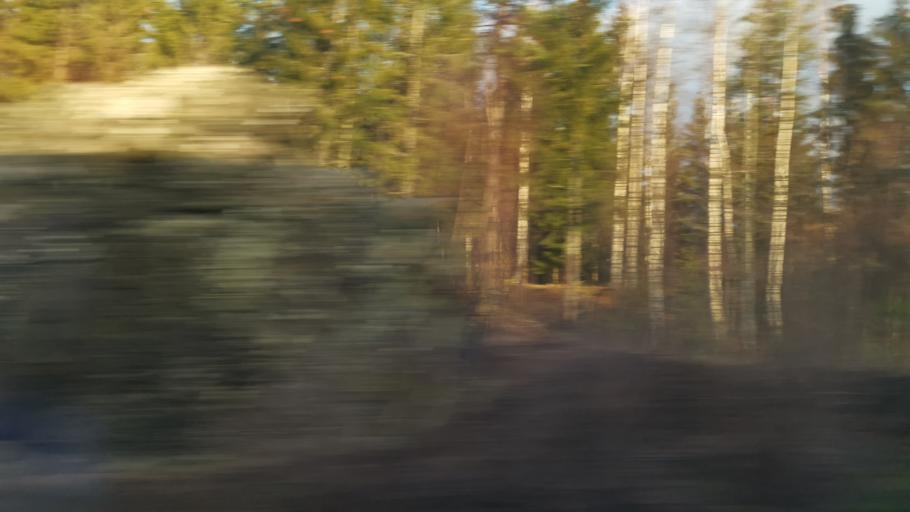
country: SE
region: Soedermanland
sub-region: Vingakers Kommun
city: Vingaker
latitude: 59.0470
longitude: 15.7675
